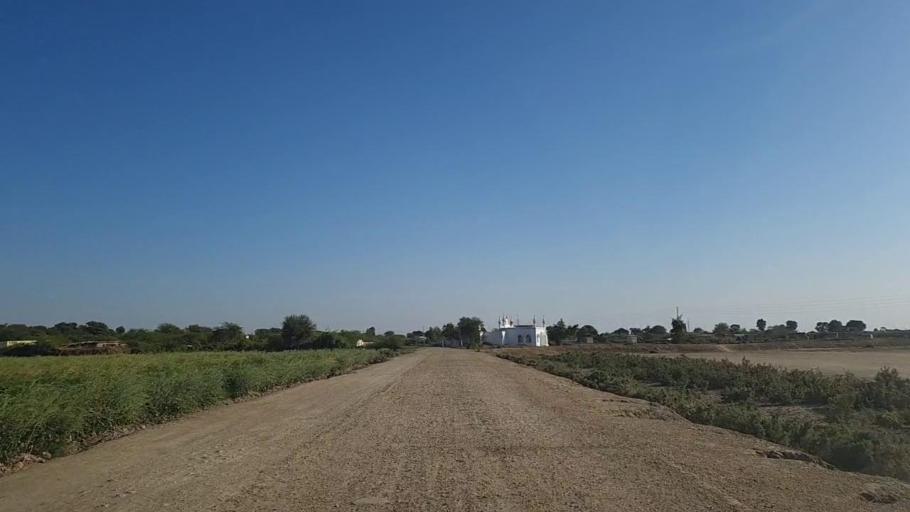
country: PK
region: Sindh
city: Samaro
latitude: 25.3024
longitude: 69.4584
